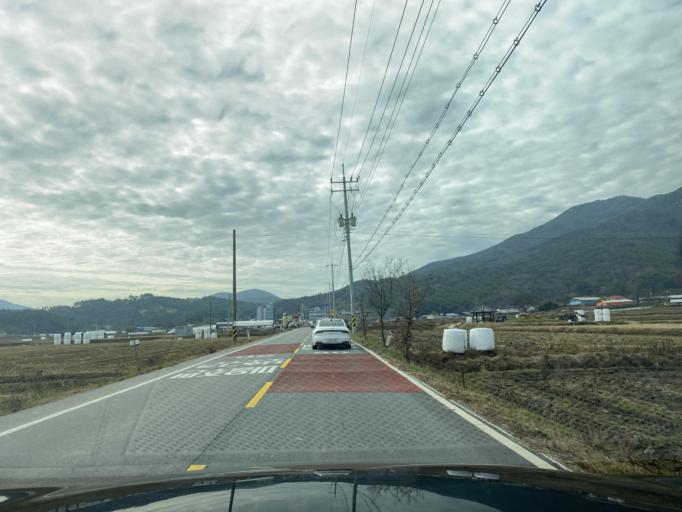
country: KR
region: Chungcheongnam-do
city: Hongsung
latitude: 36.6802
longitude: 126.6464
